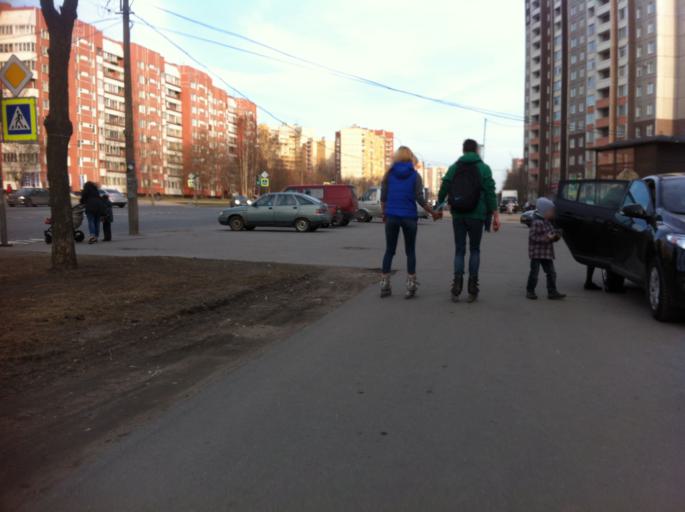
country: RU
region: St.-Petersburg
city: Uritsk
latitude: 59.8554
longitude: 30.1848
